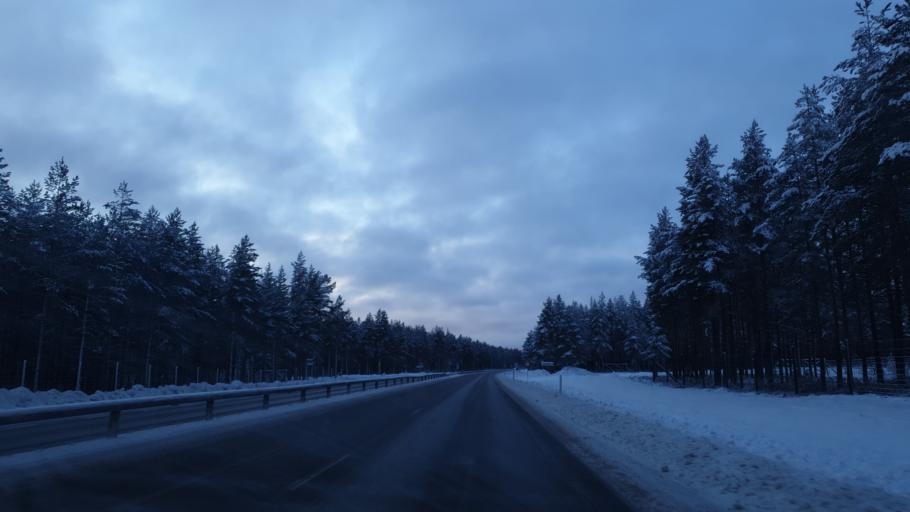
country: SE
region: Vaesterbotten
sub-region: Nordmalings Kommun
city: Nordmaling
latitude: 63.5930
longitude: 19.7040
